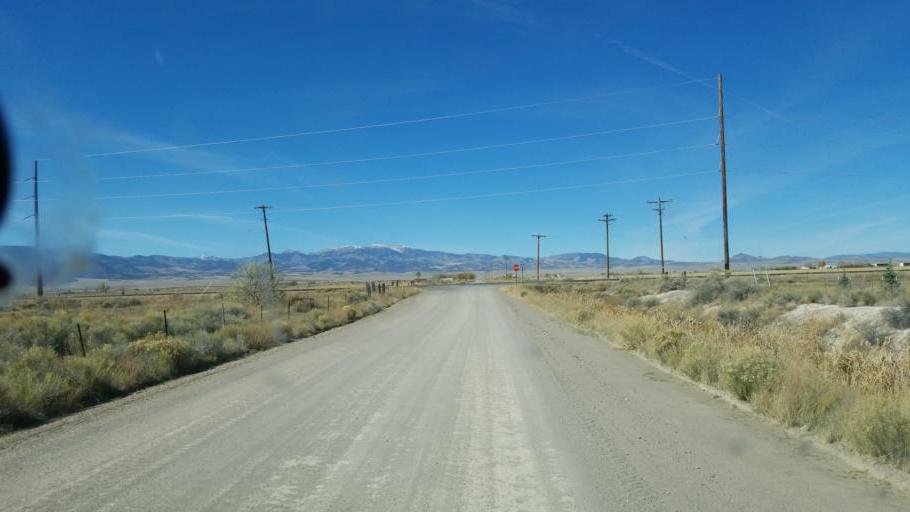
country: US
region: Colorado
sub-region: Rio Grande County
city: Monte Vista
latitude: 37.5314
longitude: -106.0931
